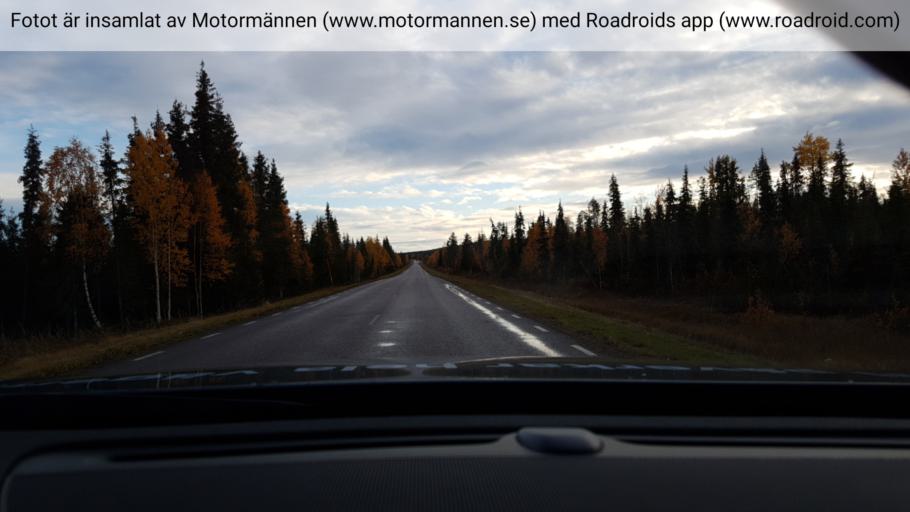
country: SE
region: Norrbotten
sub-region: Overkalix Kommun
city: OEverkalix
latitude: 66.8781
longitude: 22.7627
